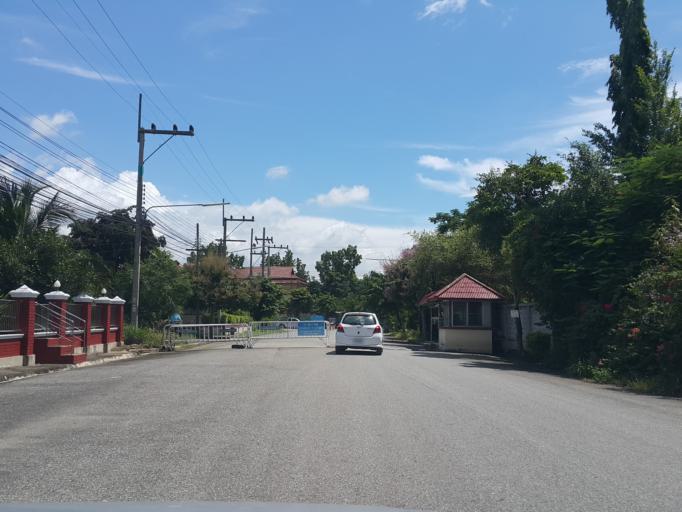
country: TH
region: Chiang Mai
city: Chiang Mai
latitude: 18.7397
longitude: 98.9646
